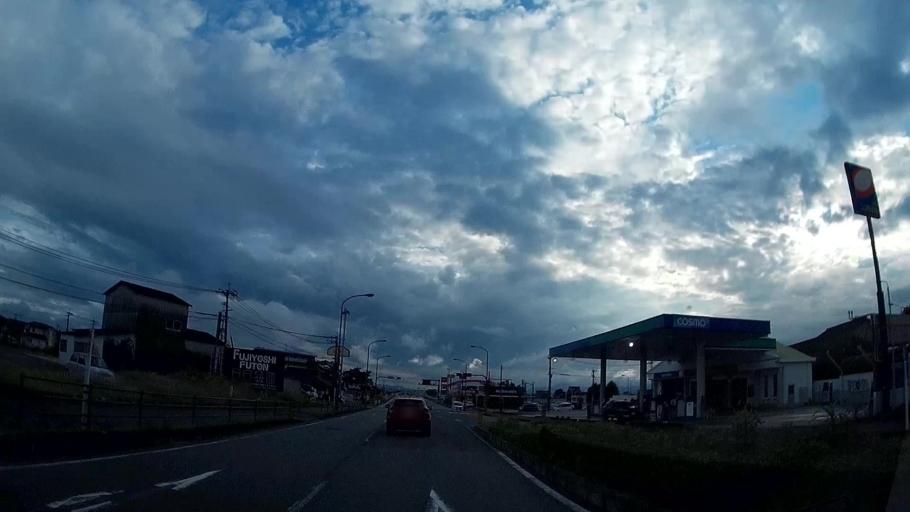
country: JP
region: Kumamoto
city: Ozu
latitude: 32.8789
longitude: 130.8873
